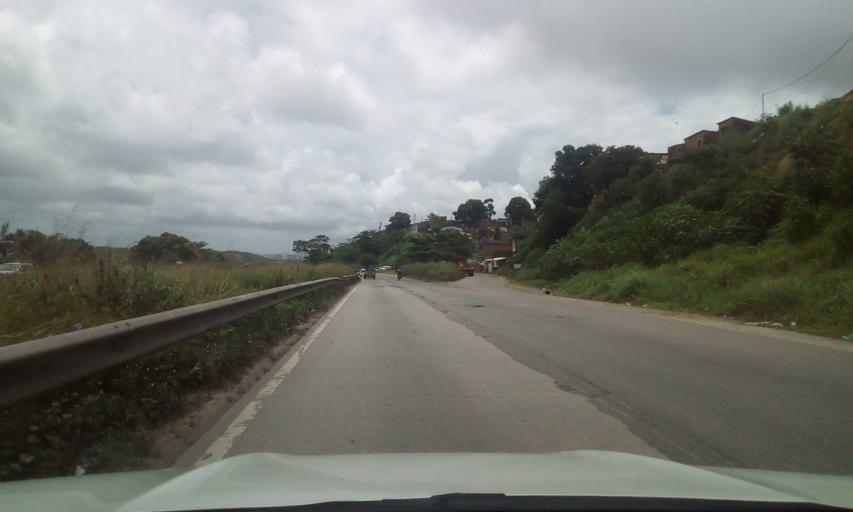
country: BR
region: Pernambuco
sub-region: Jaboatao Dos Guararapes
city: Jaboatao dos Guararapes
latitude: -8.1226
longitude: -34.9433
